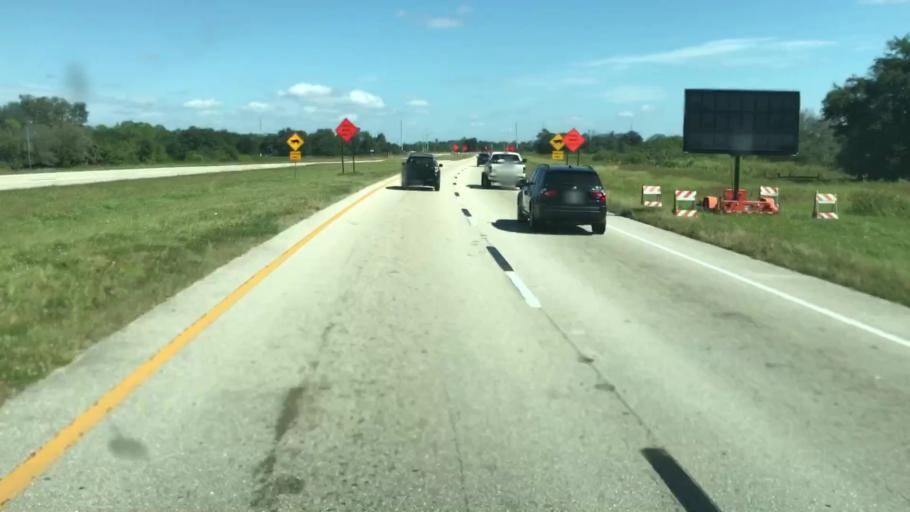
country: US
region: Florida
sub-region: Lee County
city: Gateway
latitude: 26.5769
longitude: -81.7203
